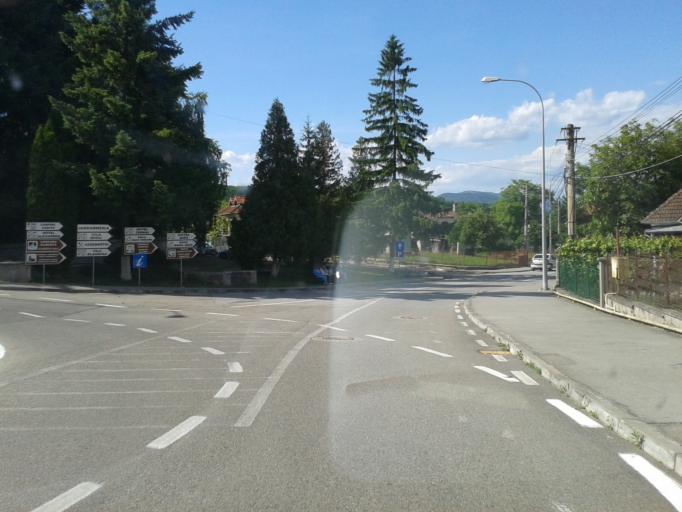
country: RO
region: Hunedoara
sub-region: Comuna Geoagiu
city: Geoagiu
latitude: 45.9345
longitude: 23.1673
